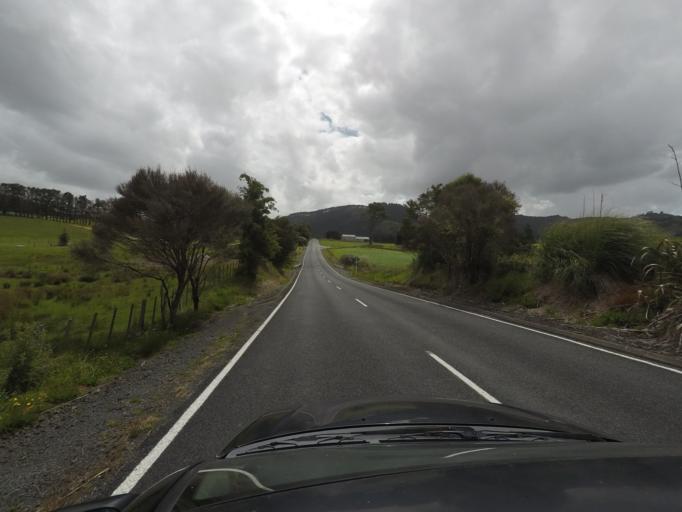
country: NZ
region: Auckland
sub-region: Auckland
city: Parakai
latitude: -36.5000
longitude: 174.4993
